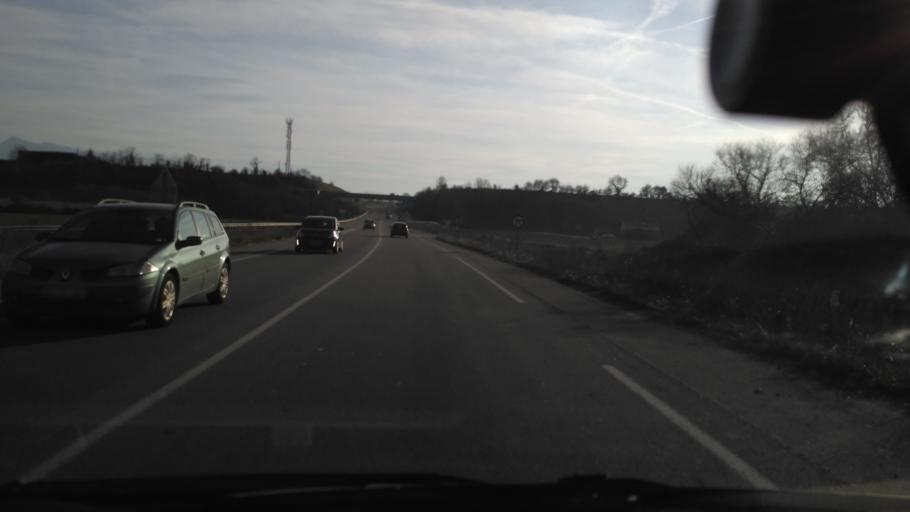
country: FR
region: Rhone-Alpes
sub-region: Departement de la Drome
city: Bourg-de-Peage
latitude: 45.0312
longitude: 5.0798
